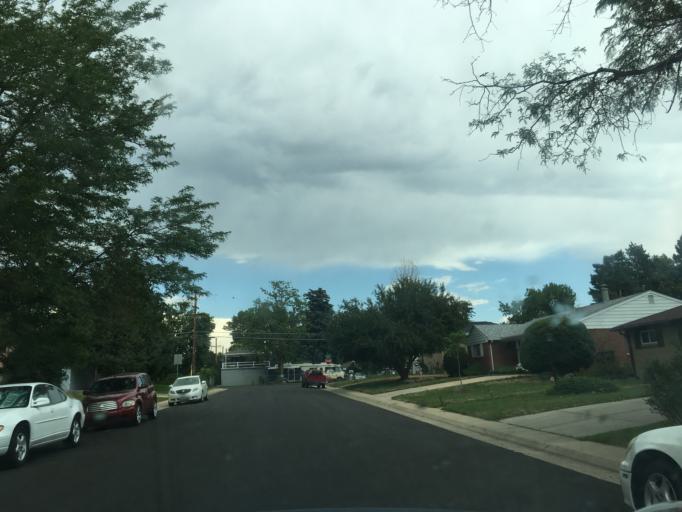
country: US
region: Colorado
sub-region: Arapahoe County
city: Sheridan
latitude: 39.6742
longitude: -105.0448
